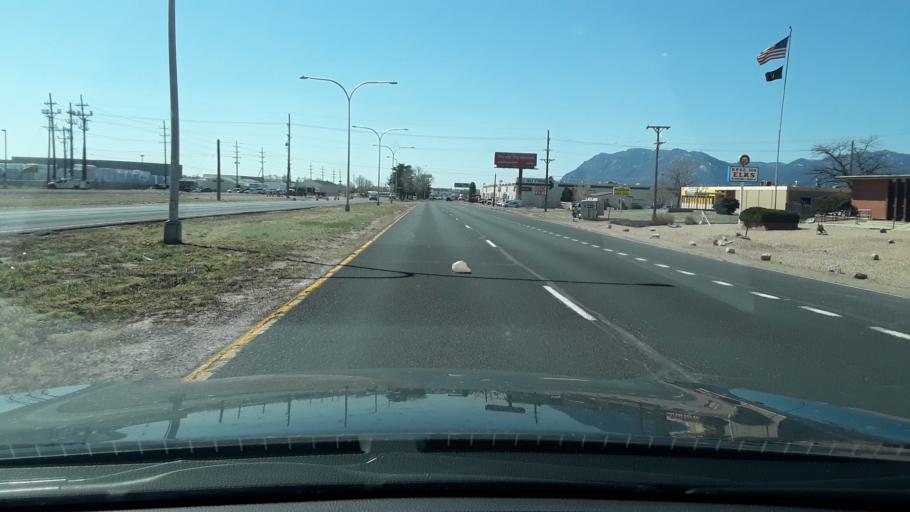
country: US
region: Colorado
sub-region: El Paso County
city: Colorado Springs
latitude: 38.8807
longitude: -104.8188
